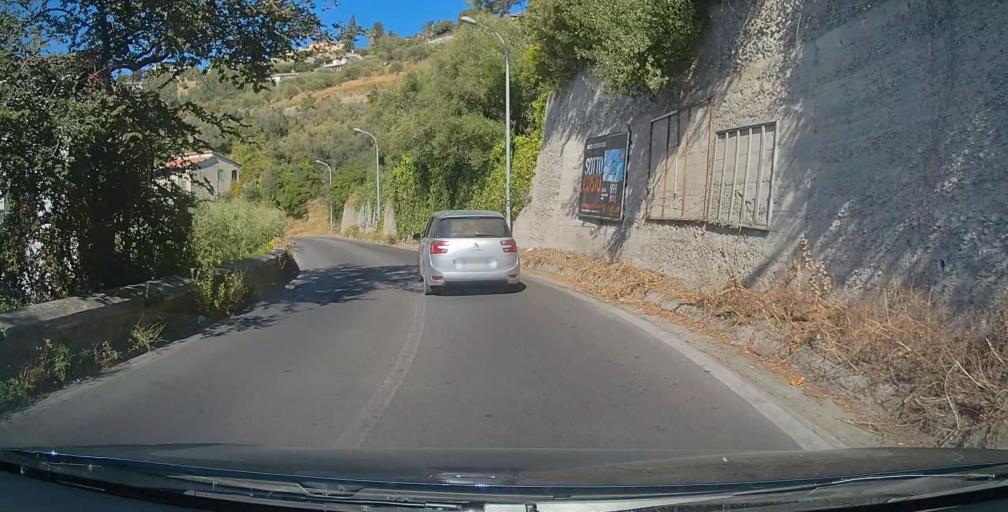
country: IT
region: Sicily
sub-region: Messina
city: Capo d'Orlando
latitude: 38.1593
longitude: 14.7487
